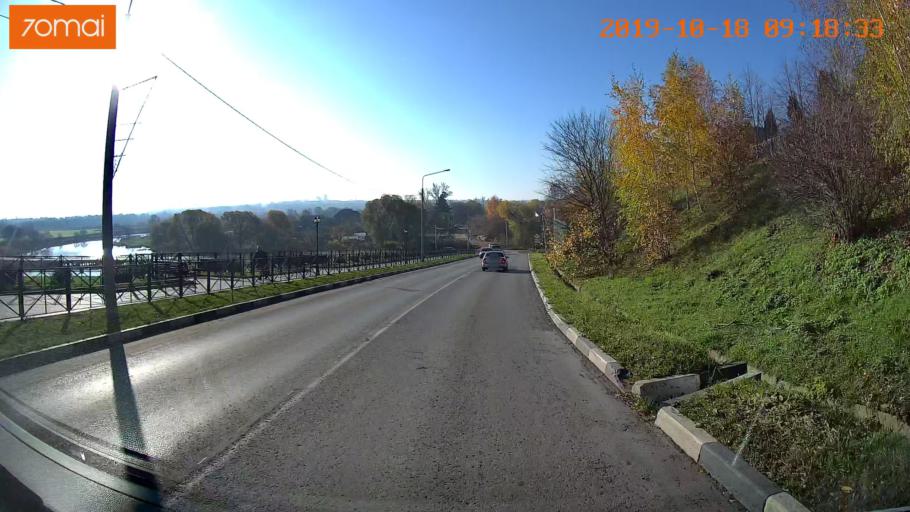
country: RU
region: Tula
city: Yefremov
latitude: 53.1363
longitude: 38.1204
